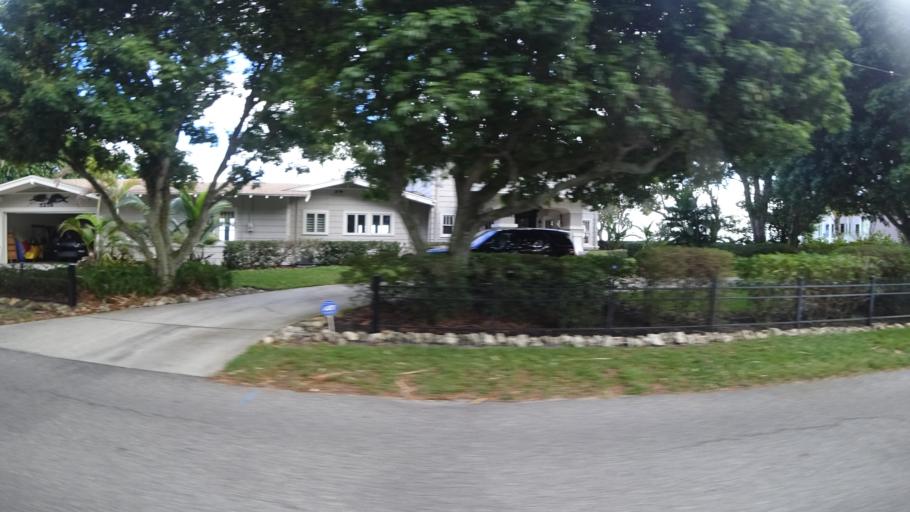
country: US
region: Florida
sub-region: Manatee County
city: West Bradenton
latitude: 27.5085
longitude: -82.6153
